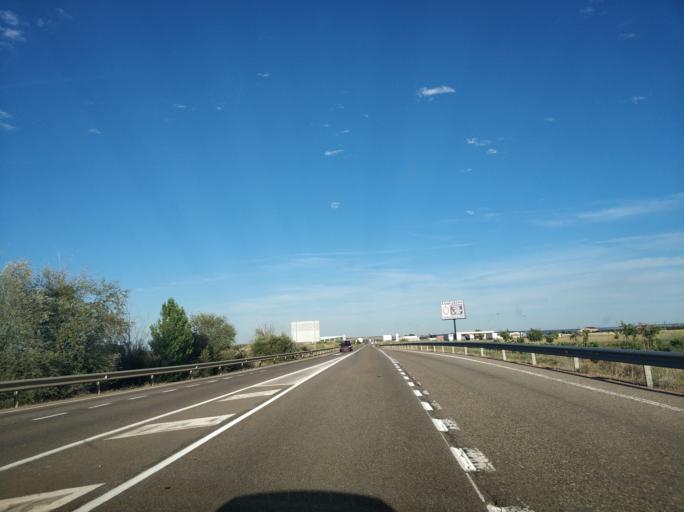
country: ES
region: Castille and Leon
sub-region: Provincia de Leon
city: Villamanan
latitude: 42.3253
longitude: -5.6054
